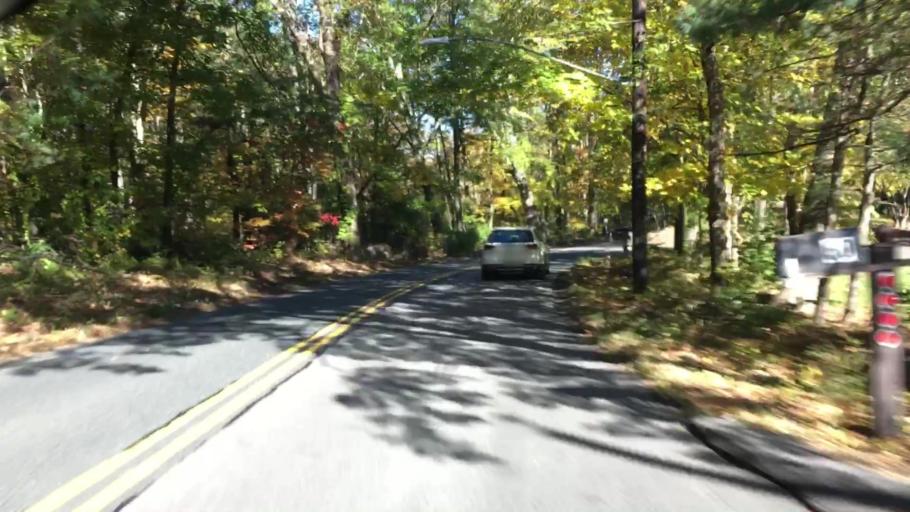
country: US
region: Massachusetts
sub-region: Middlesex County
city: Ashland
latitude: 42.2804
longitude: -71.4609
